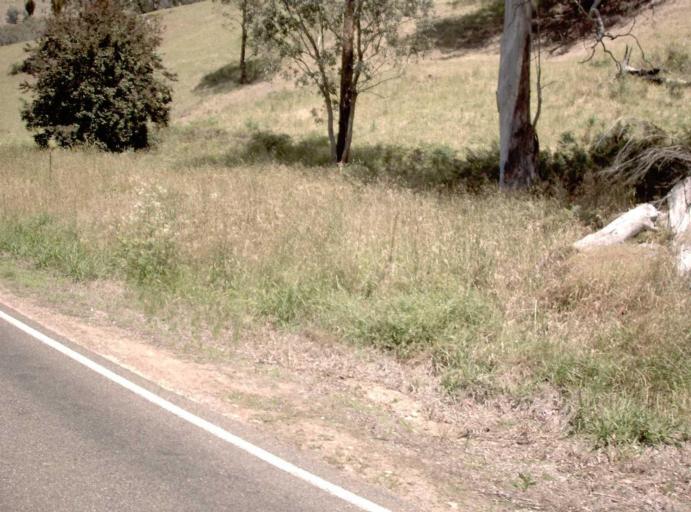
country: AU
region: Victoria
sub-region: East Gippsland
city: Bairnsdale
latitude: -37.4093
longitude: 147.8356
